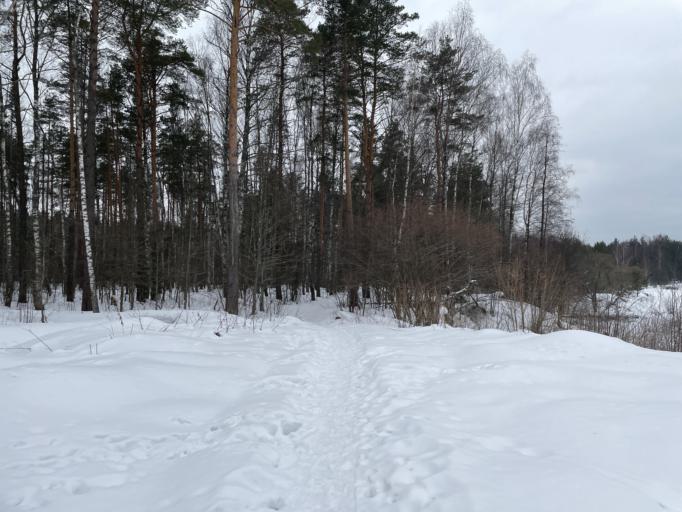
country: RU
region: Vladimir
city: Pokrov
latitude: 55.9426
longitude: 39.2395
